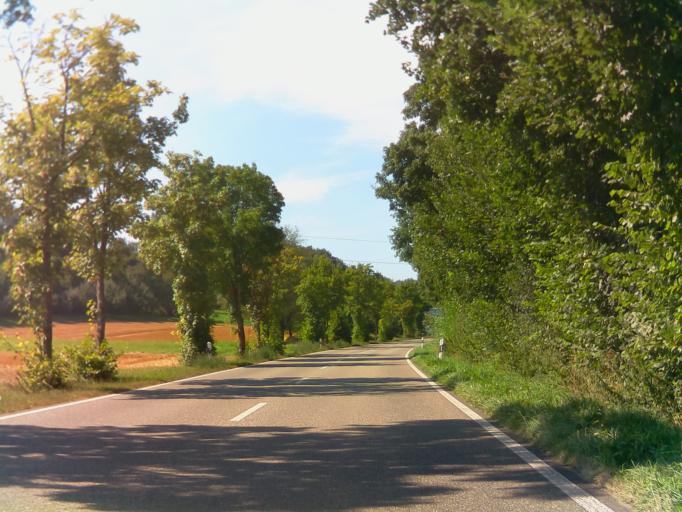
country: DE
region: Baden-Wuerttemberg
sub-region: Karlsruhe Region
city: Oberderdingen
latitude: 49.0977
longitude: 8.7472
